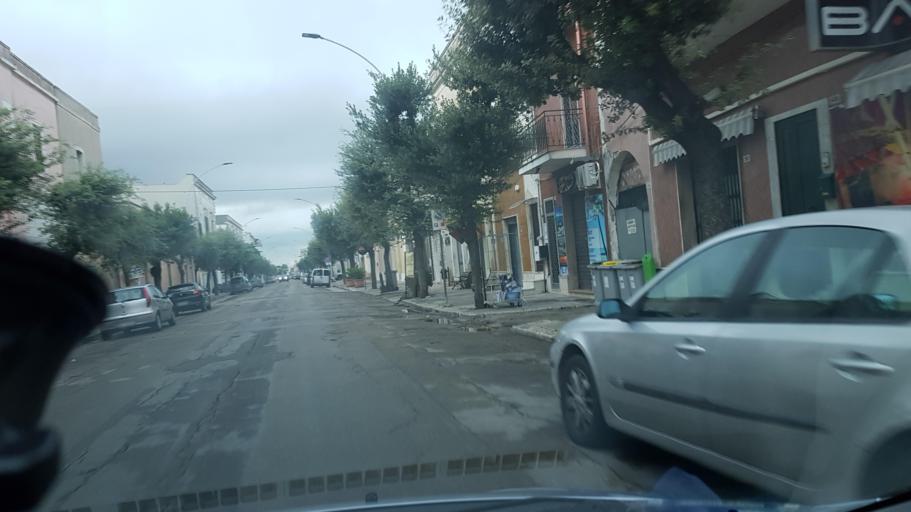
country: IT
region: Apulia
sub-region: Provincia di Lecce
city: Carmiano
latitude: 40.3469
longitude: 18.0453
